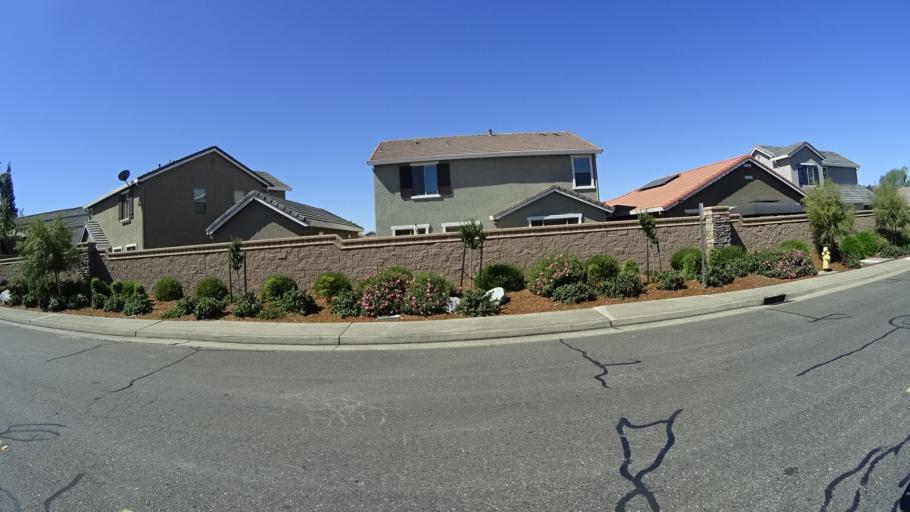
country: US
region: California
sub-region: Placer County
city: Rocklin
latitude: 38.8000
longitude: -121.2136
